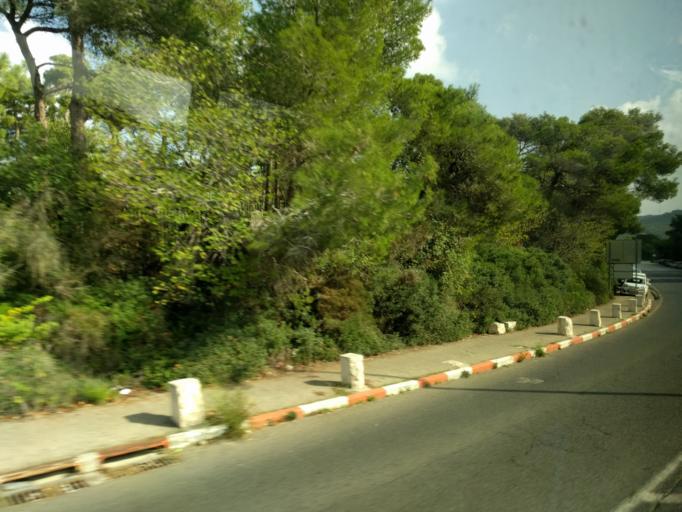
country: IL
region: Haifa
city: Nesher
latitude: 32.7583
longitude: 35.0213
